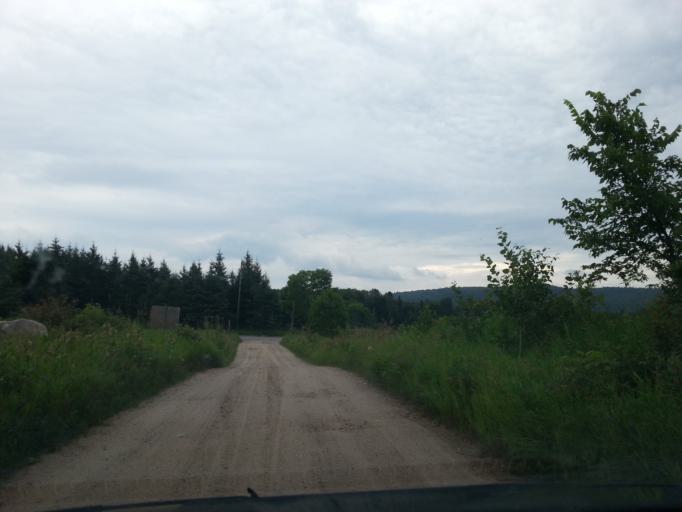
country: CA
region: Quebec
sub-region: Outaouais
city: Maniwaki
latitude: 46.1994
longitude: -76.1330
